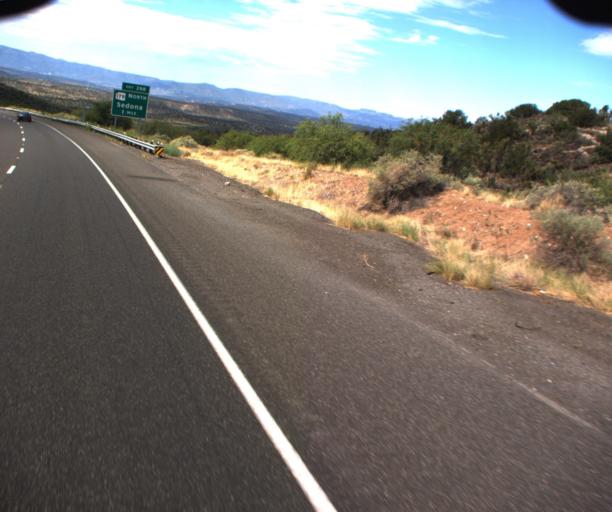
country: US
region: Arizona
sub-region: Yavapai County
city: Big Park
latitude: 34.7074
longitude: -111.7415
